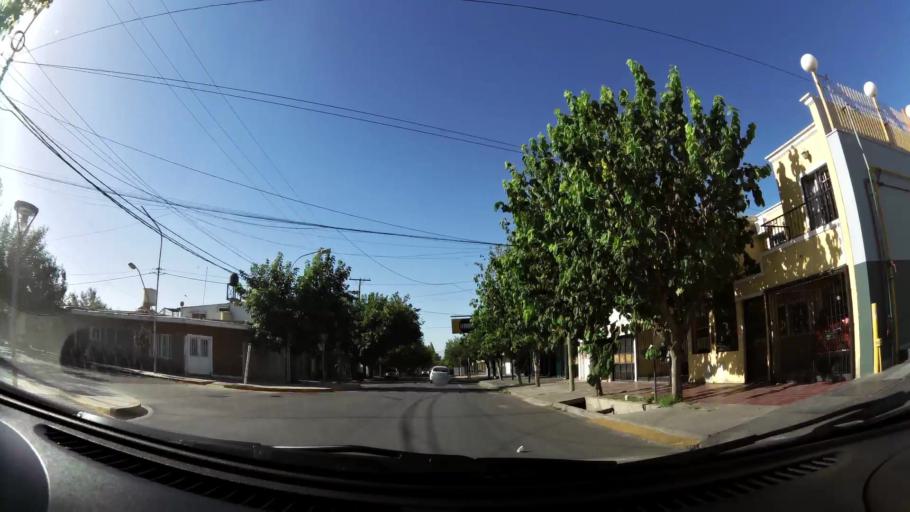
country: AR
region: Mendoza
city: Villa Nueva
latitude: -32.9126
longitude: -68.7974
